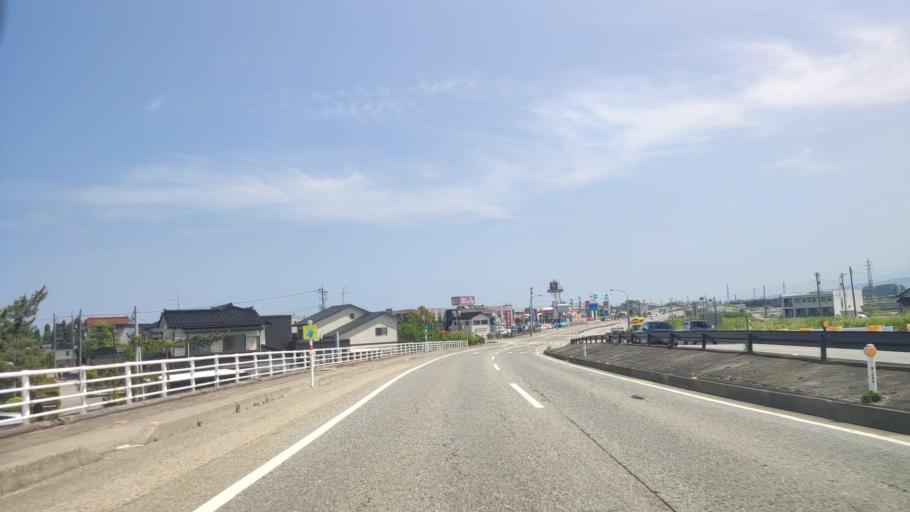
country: JP
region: Toyama
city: Namerikawa
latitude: 36.7544
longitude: 137.3575
